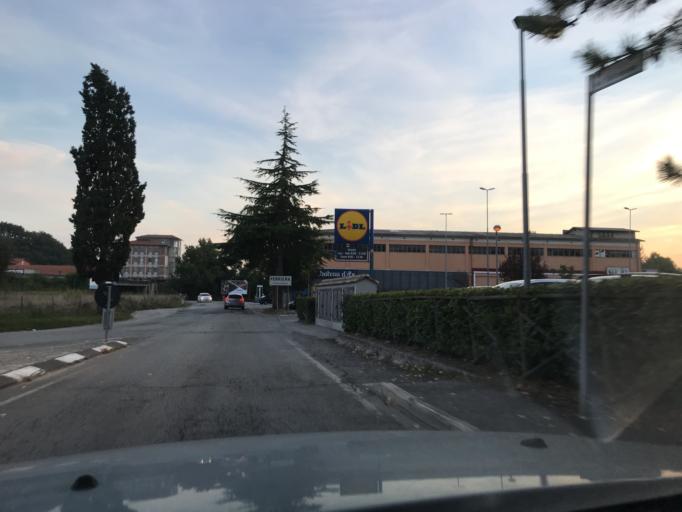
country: IT
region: Umbria
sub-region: Provincia di Perugia
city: Via Lippia
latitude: 43.0902
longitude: 12.4506
